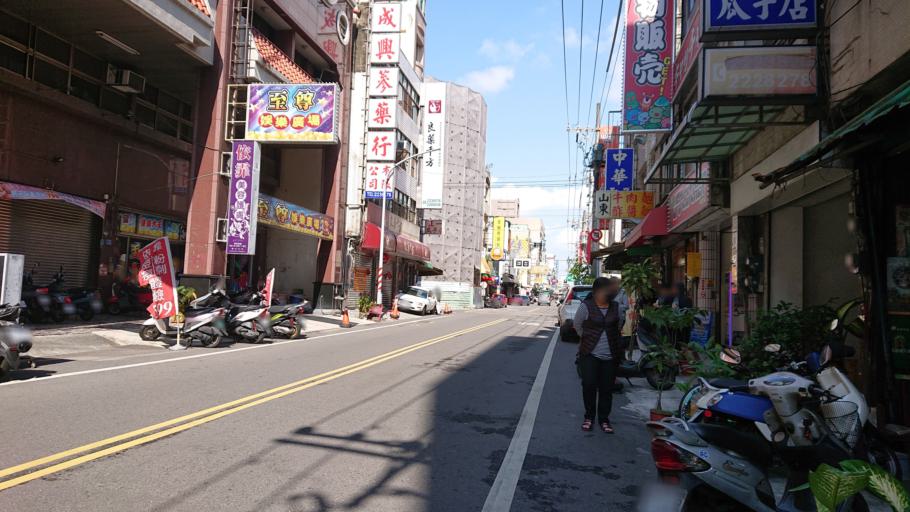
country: TW
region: Taiwan
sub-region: Chiayi
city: Jiayi Shi
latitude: 23.4766
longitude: 120.4445
